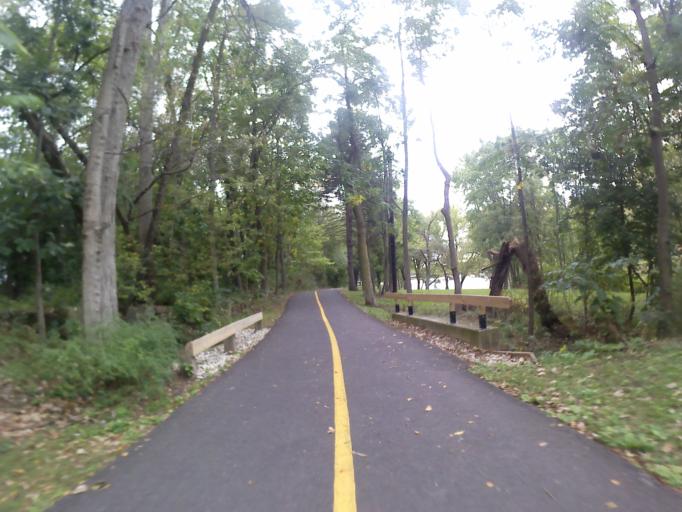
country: US
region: Illinois
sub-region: Kane County
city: North Aurora
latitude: 41.8035
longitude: -88.3245
